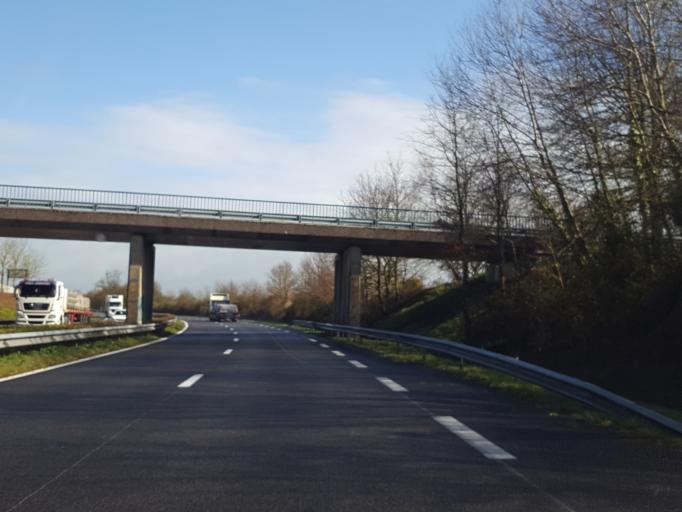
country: FR
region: Pays de la Loire
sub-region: Departement de la Vendee
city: Belleville-sur-Vie
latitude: 46.7775
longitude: -1.4206
